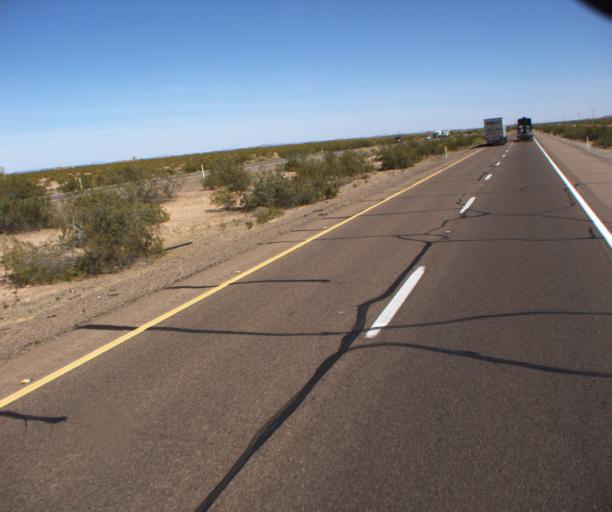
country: US
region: Arizona
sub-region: Yuma County
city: Wellton
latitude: 32.7713
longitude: -113.6074
